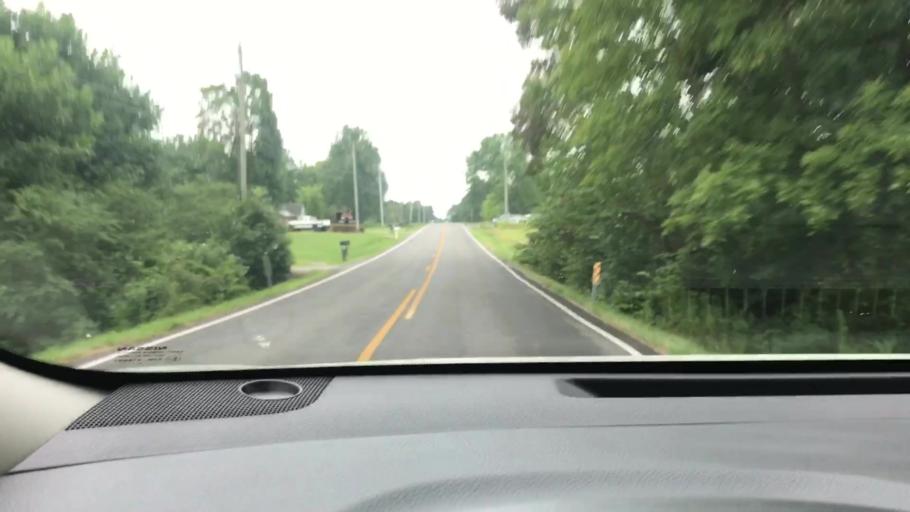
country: US
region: Kentucky
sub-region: Calloway County
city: Murray
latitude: 36.6847
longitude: -88.2992
